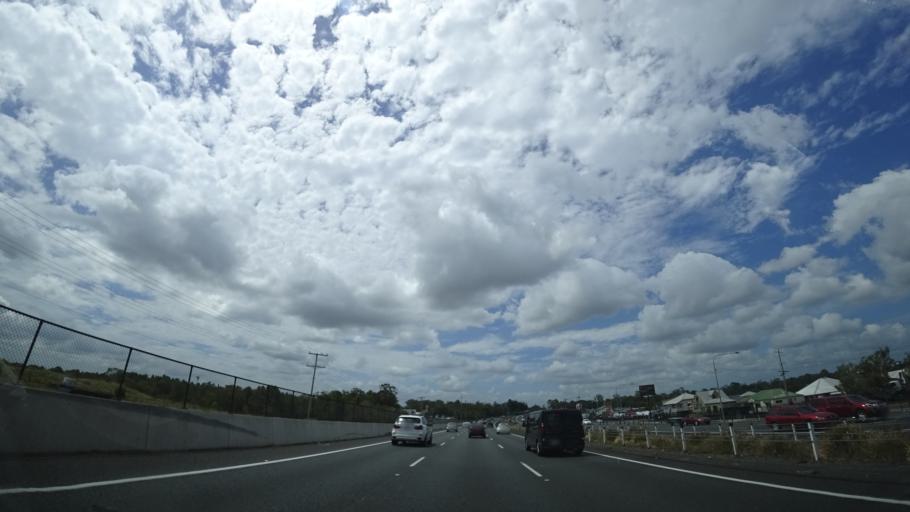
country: AU
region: Queensland
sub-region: Moreton Bay
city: Burpengary
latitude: -27.1593
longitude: 152.9781
